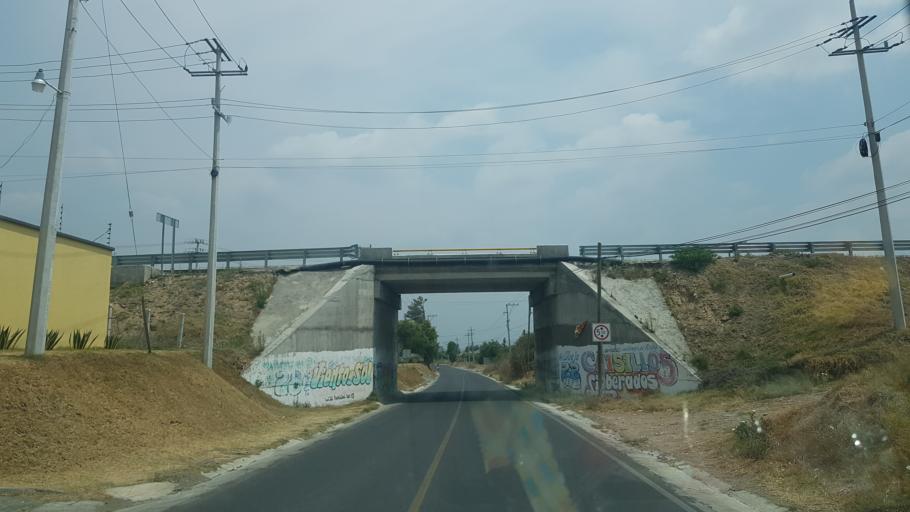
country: MX
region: Puebla
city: Huejotzingo
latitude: 19.1429
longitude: -98.4112
